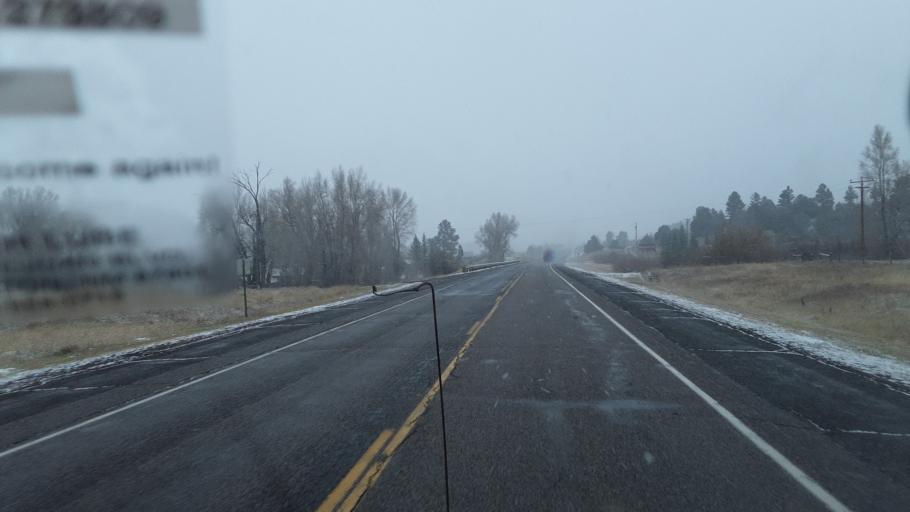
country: US
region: New Mexico
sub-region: Rio Arriba County
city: Chama
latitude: 36.8137
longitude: -106.5684
